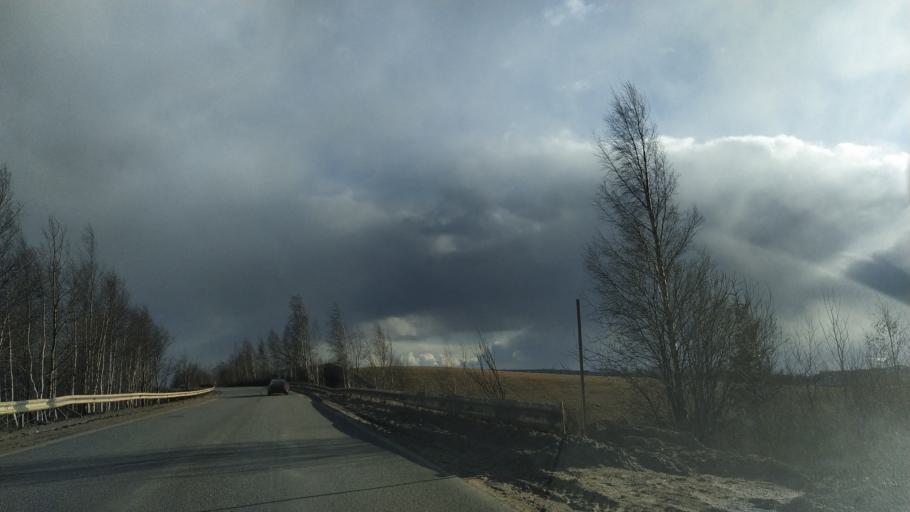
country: RU
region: Leningrad
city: Bugry
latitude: 60.0966
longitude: 30.3900
